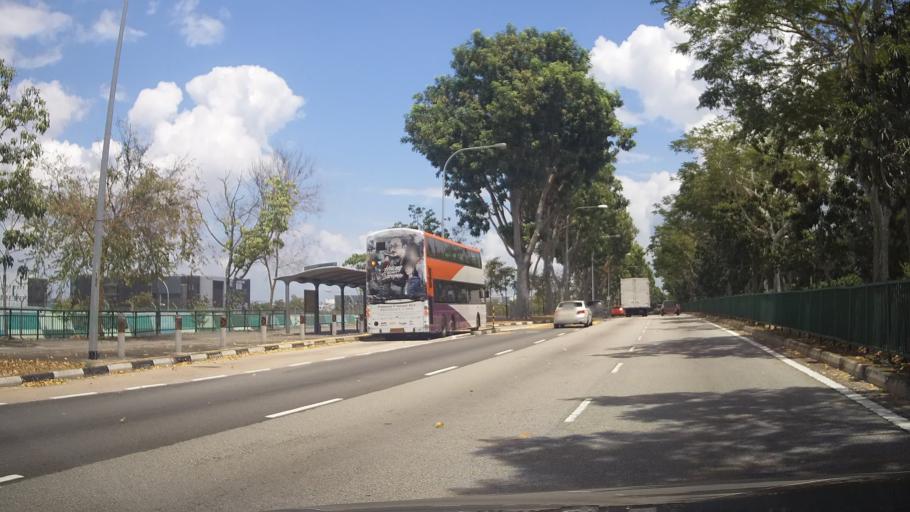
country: MY
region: Johor
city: Kampung Pasir Gudang Baru
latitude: 1.3668
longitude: 103.9676
